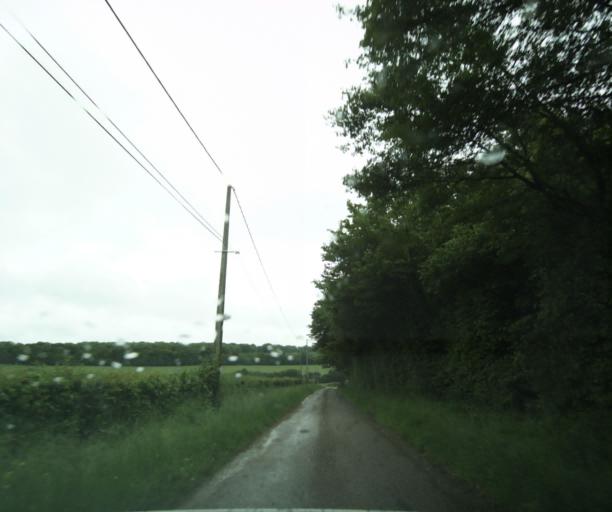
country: FR
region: Bourgogne
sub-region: Departement de Saone-et-Loire
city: Charolles
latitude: 46.4879
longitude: 4.2891
